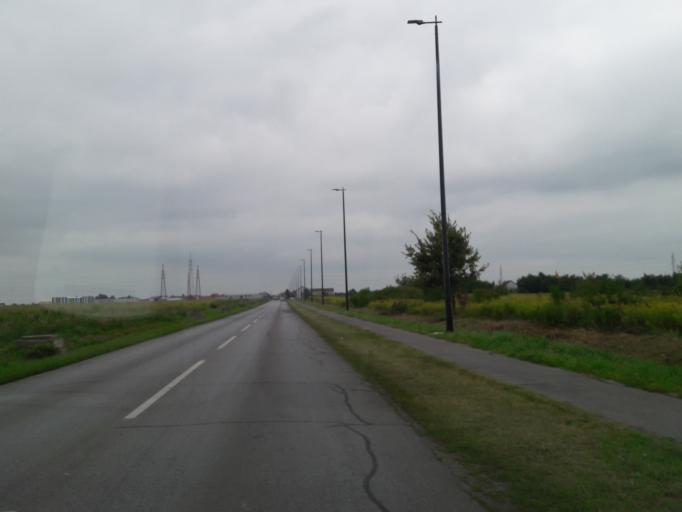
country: HR
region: Osjecko-Baranjska
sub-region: Grad Osijek
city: Osijek
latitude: 45.5268
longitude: 18.7227
